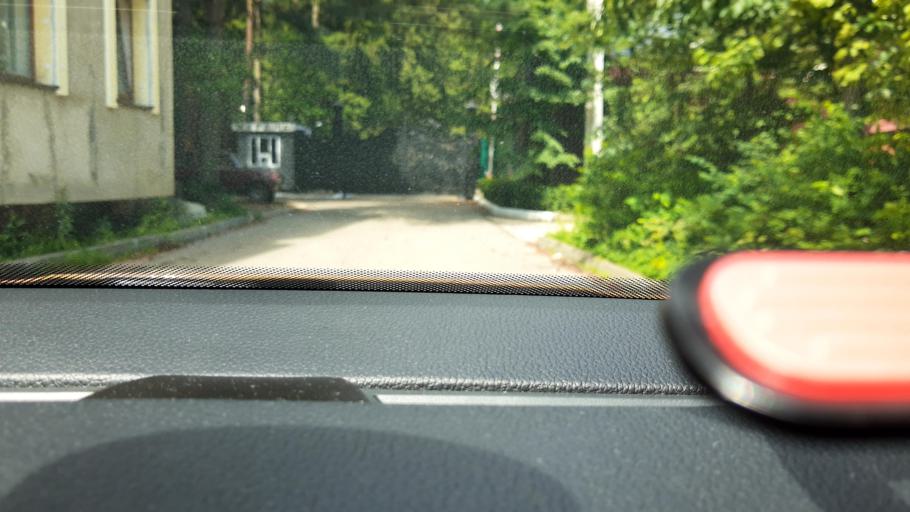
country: RU
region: Moskovskaya
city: Firsanovka
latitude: 55.9063
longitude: 37.2160
